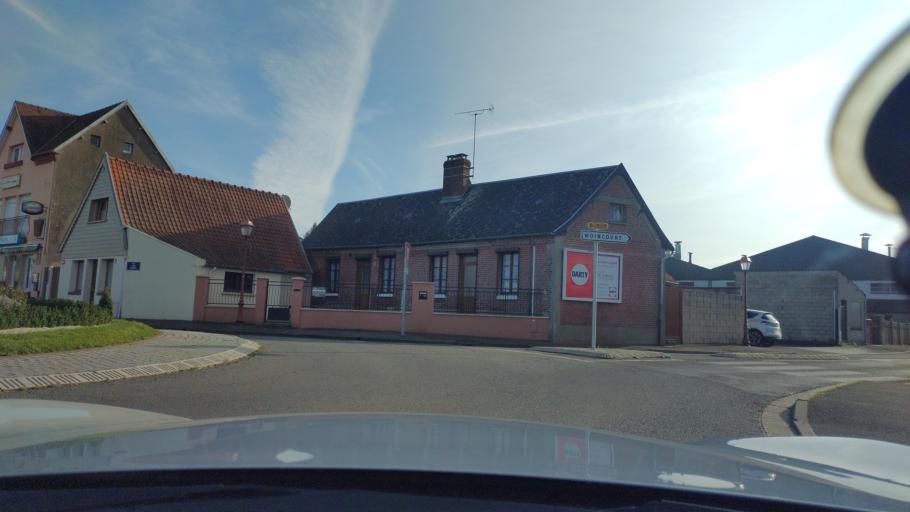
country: FR
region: Picardie
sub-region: Departement de la Somme
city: Fressenneville
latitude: 50.0680
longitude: 1.5708
